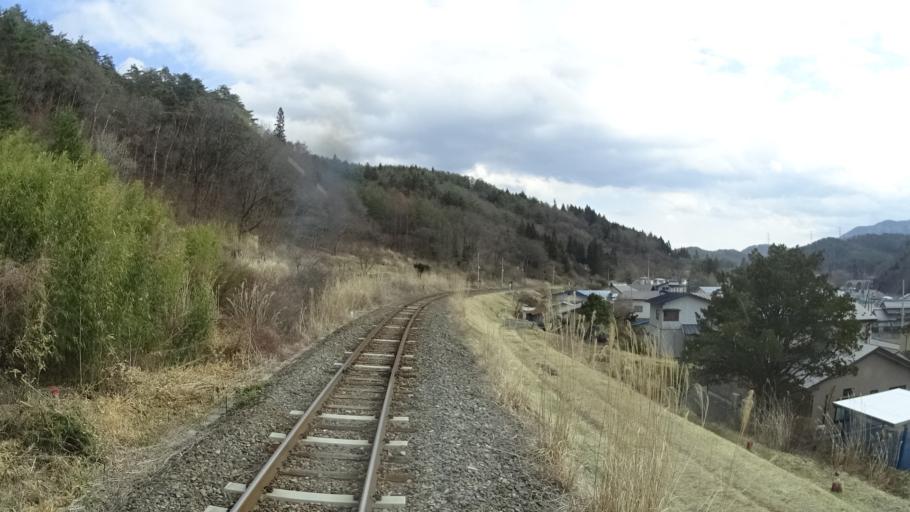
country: JP
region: Iwate
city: Tono
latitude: 39.3531
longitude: 141.3490
